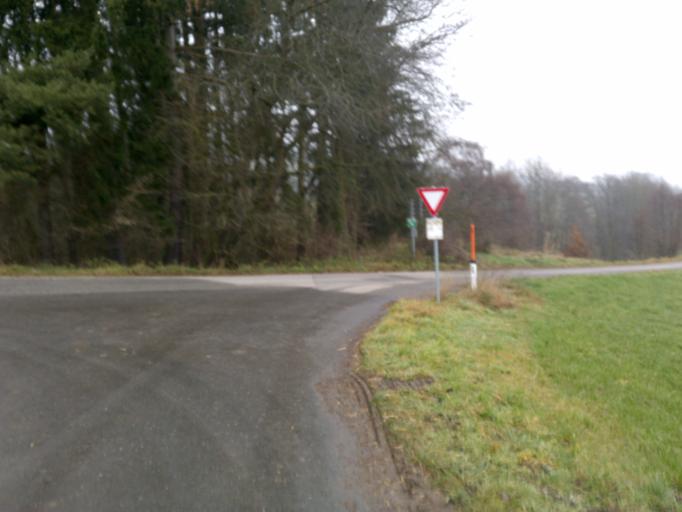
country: AT
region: Styria
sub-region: Politischer Bezirk Murtal
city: Feistritz bei Knittelfeld
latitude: 47.2911
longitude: 14.8981
